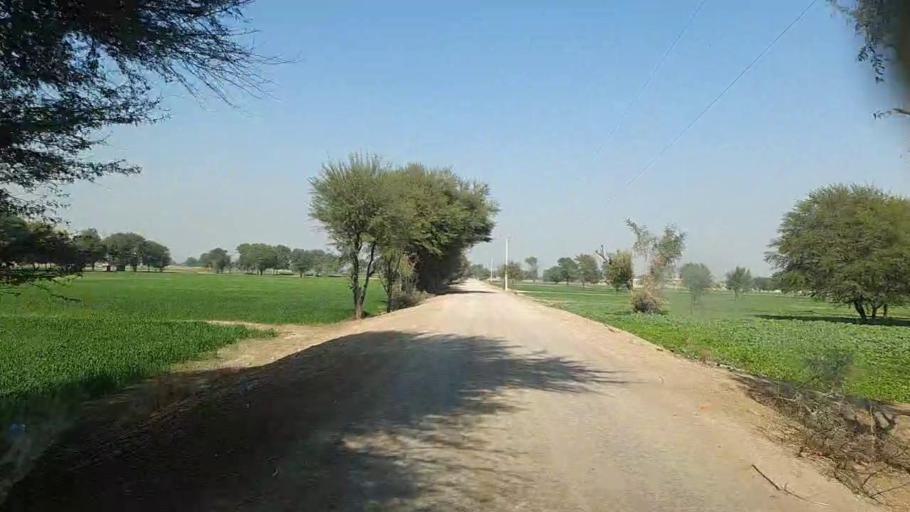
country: PK
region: Sindh
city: Khairpur
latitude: 27.9987
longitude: 69.8498
